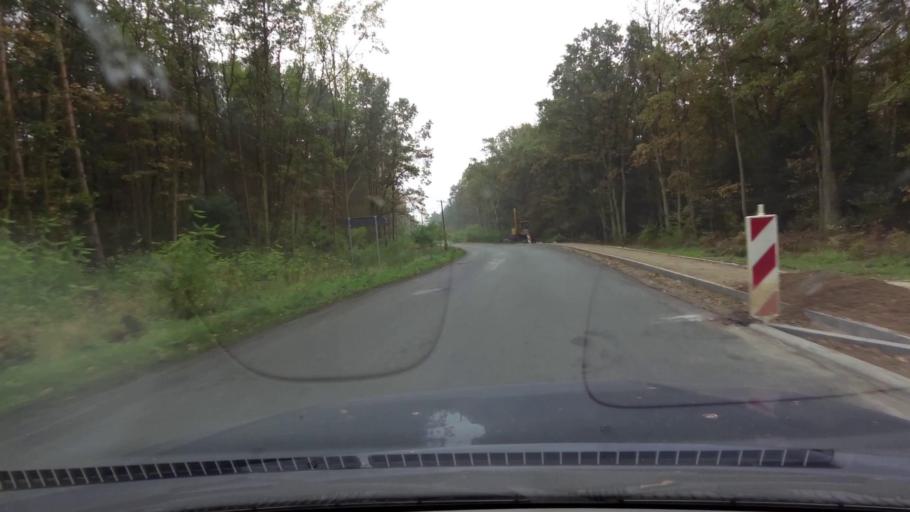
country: PL
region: West Pomeranian Voivodeship
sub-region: Powiat goleniowski
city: Goleniow
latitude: 53.5509
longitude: 14.7756
